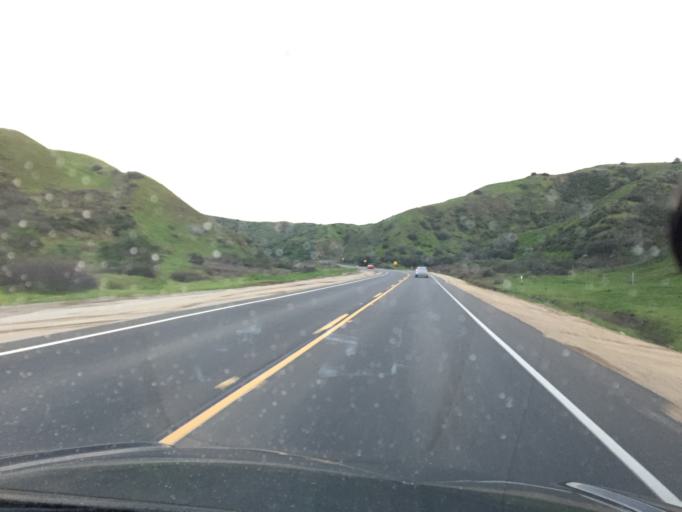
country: US
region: California
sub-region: San Bernardino County
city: Redlands
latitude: 33.9809
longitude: -117.1557
